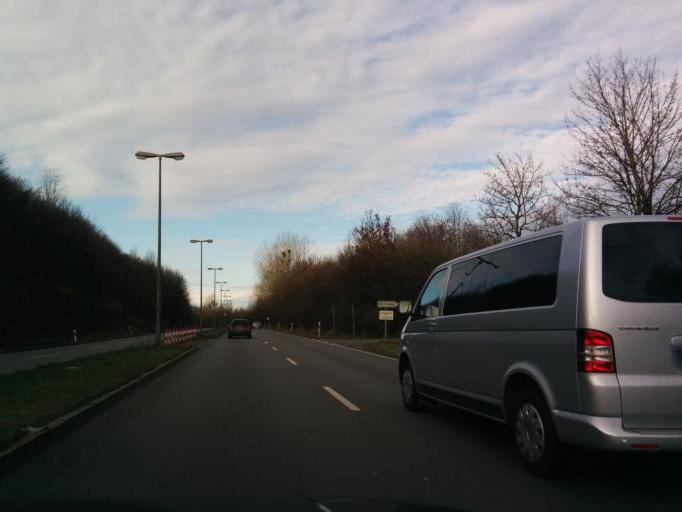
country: DE
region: Bavaria
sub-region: Upper Bavaria
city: Karlsfeld
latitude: 48.1922
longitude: 11.5102
